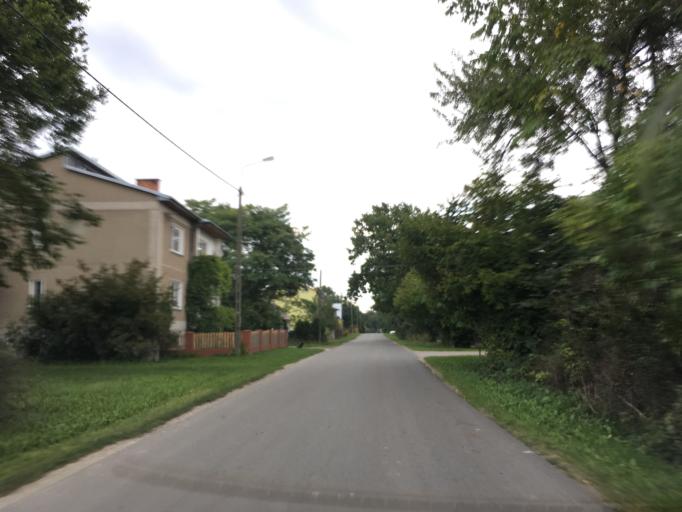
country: PL
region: Lesser Poland Voivodeship
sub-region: Powiat olkuski
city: Wolbrom
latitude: 50.4812
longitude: 19.8283
